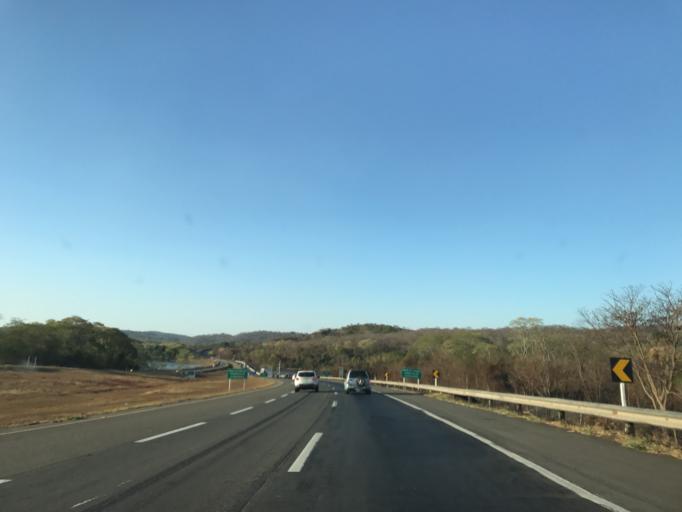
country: BR
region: Goias
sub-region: Goianapolis
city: Goianapolis
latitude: -16.5458
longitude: -49.1506
